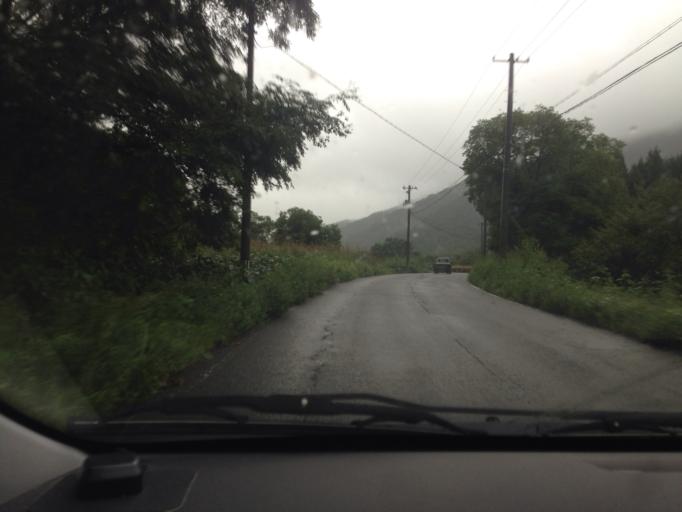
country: JP
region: Fukushima
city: Inawashiro
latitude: 37.3978
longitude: 140.1418
